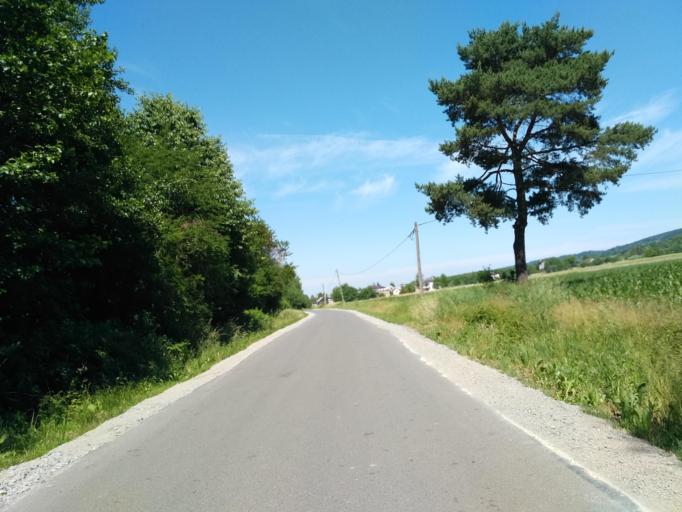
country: PL
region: Subcarpathian Voivodeship
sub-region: Powiat krosnienski
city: Korczyna
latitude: 49.7174
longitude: 21.7821
